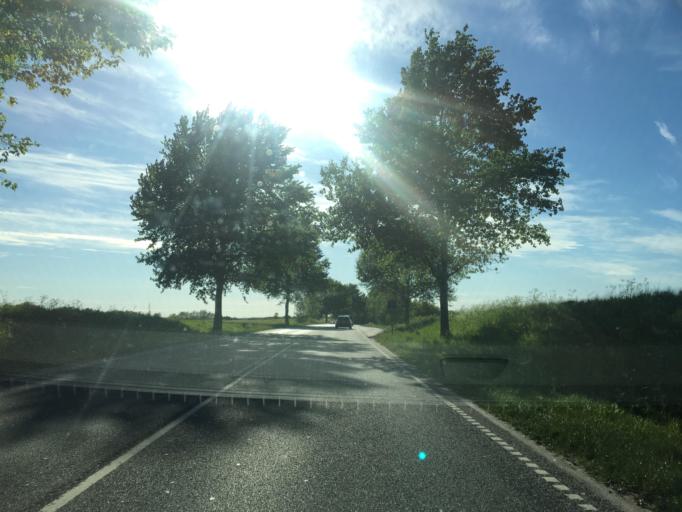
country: DK
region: Capital Region
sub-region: Frederikssund Kommune
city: Slangerup
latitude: 55.8349
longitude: 12.1753
